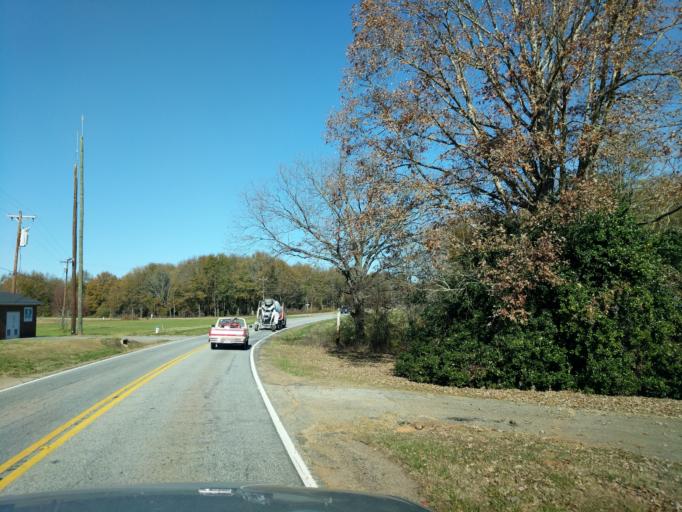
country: US
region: South Carolina
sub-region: Spartanburg County
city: Duncan
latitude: 34.9971
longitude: -82.1779
